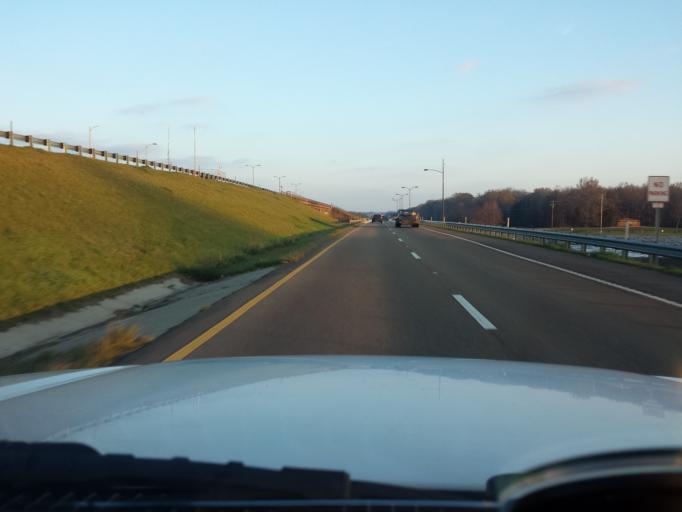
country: US
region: Mississippi
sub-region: Madison County
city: Ridgeland
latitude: 32.3980
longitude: -90.0659
